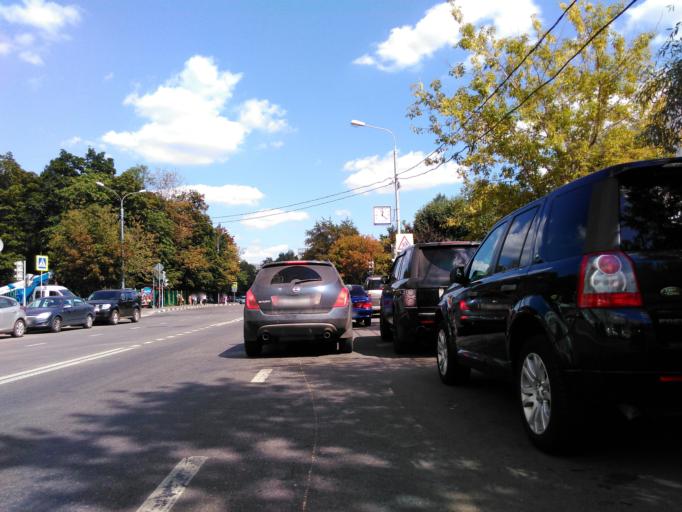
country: RU
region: Moskovskaya
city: Semenovskoye
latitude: 55.6619
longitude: 37.5245
